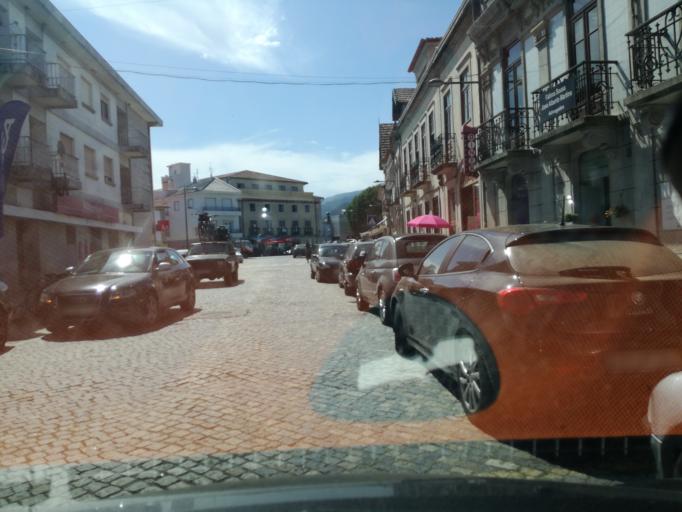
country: ES
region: Galicia
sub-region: Provincia de Pontevedra
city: A Guarda
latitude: 41.8782
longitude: -8.8373
